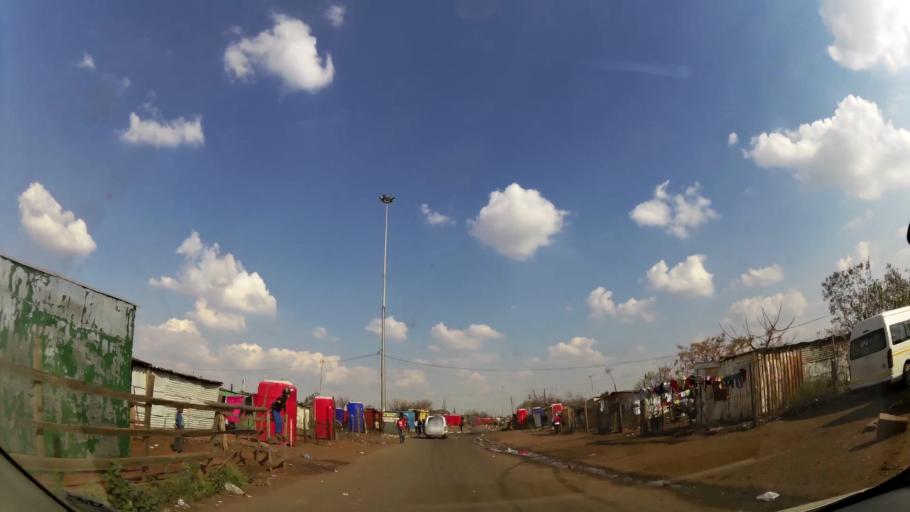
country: ZA
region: Gauteng
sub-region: Ekurhuleni Metropolitan Municipality
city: Germiston
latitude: -26.3302
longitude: 28.1412
